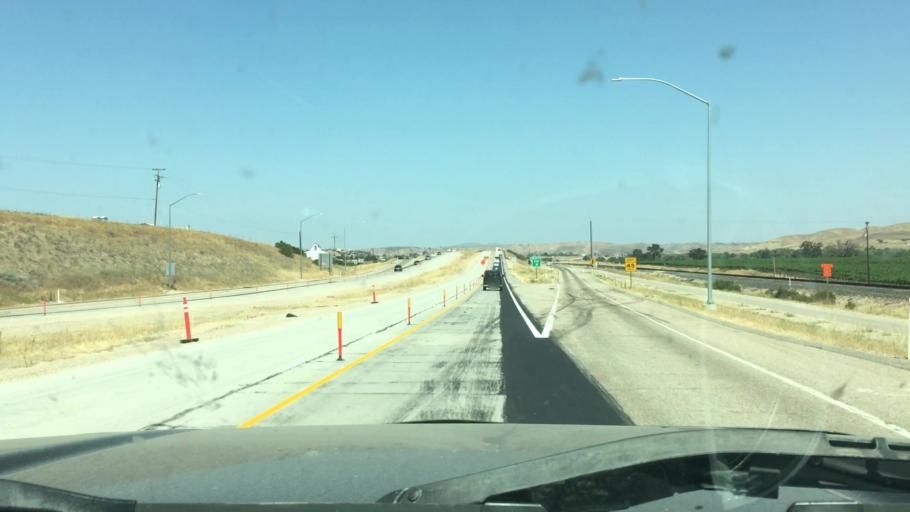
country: US
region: California
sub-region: San Luis Obispo County
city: San Miguel
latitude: 35.7724
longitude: -120.7072
